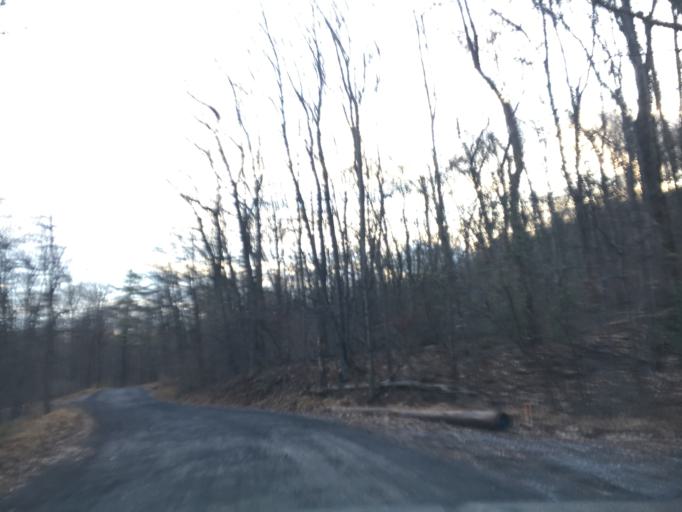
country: US
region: Pennsylvania
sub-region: Carbon County
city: Lehighton
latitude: 40.7641
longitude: -75.6934
